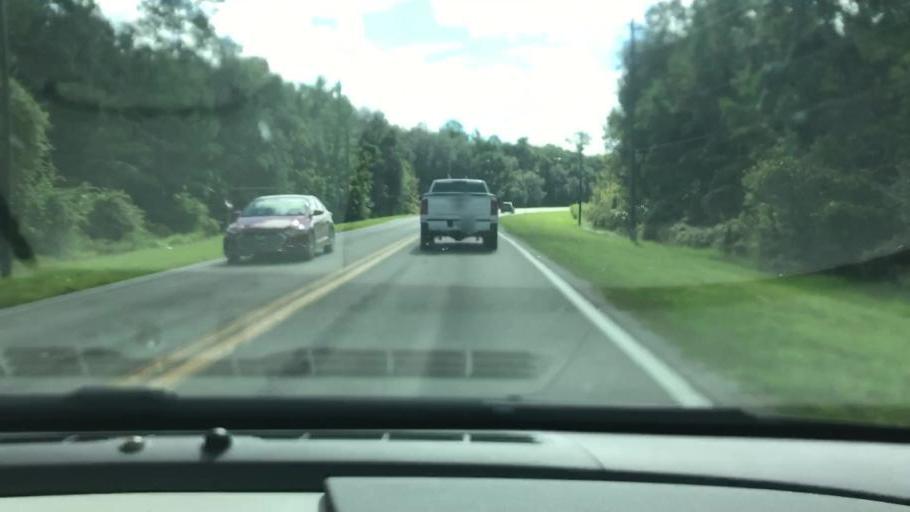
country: US
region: Florida
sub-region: Alachua County
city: Gainesville
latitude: 29.6496
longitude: -82.4054
